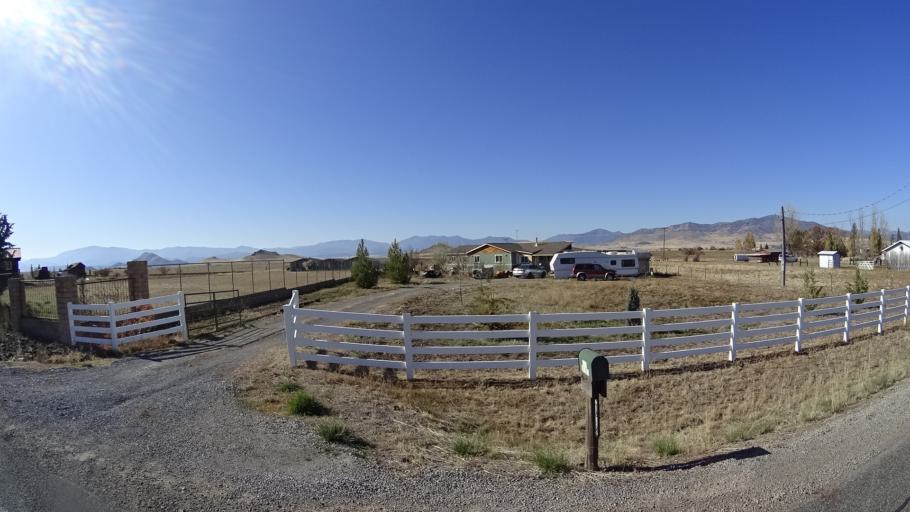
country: US
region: California
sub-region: Siskiyou County
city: Montague
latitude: 41.7513
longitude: -122.4572
